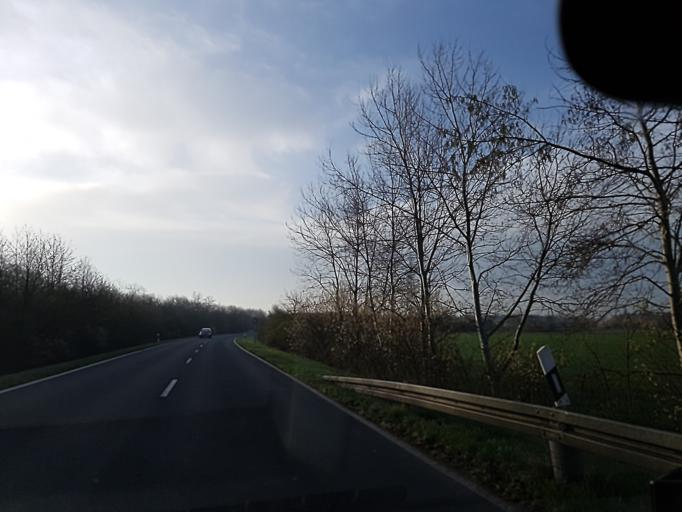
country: DE
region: Saxony
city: Riesa
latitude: 51.3401
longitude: 13.3035
